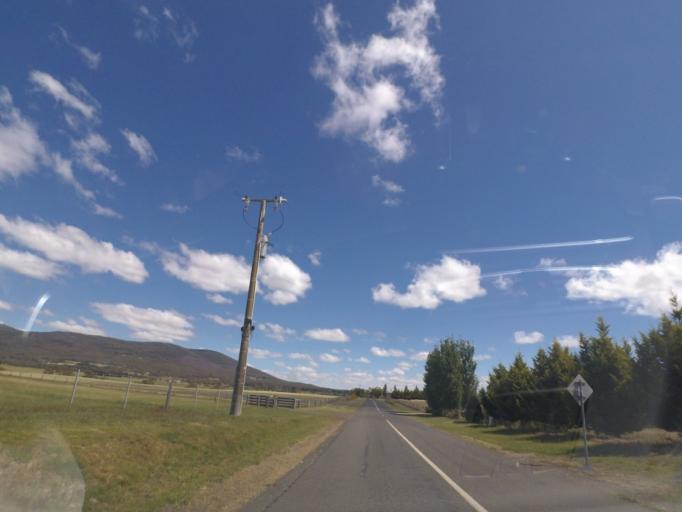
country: AU
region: Victoria
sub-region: Hume
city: Sunbury
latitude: -37.3356
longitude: 144.5581
